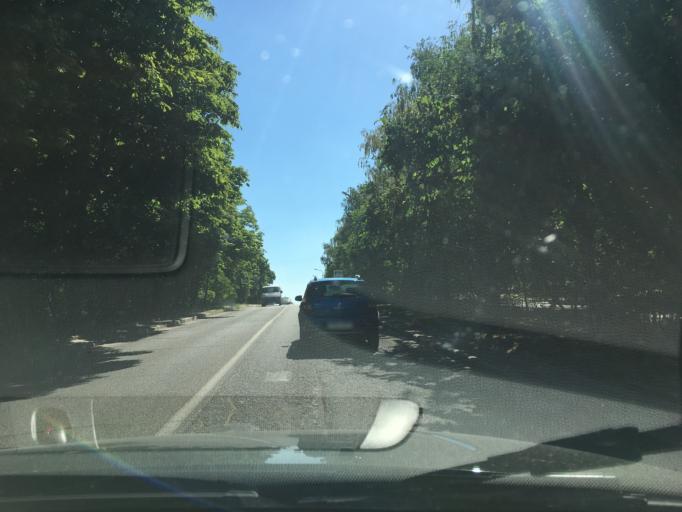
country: BY
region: Grodnenskaya
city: Hrodna
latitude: 53.6949
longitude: 23.8470
